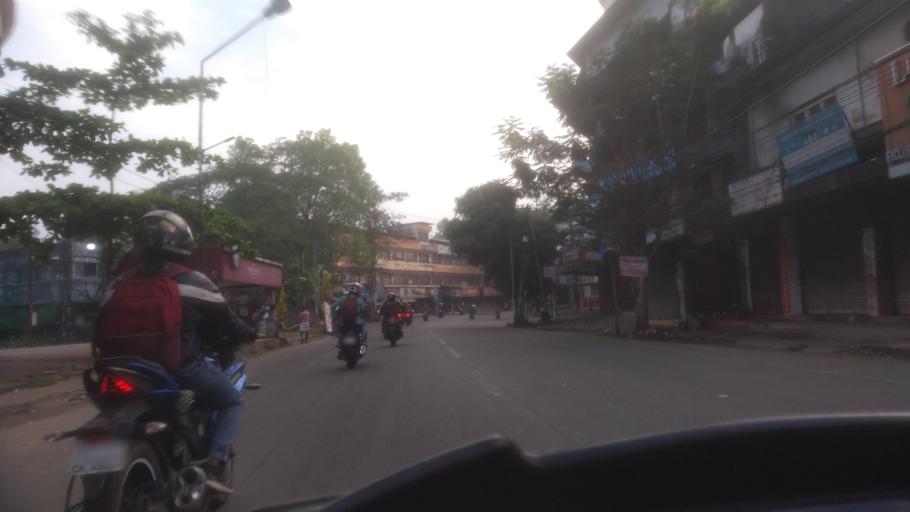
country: IN
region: Kerala
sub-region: Ernakulam
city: Aluva
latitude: 10.1125
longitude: 76.3532
